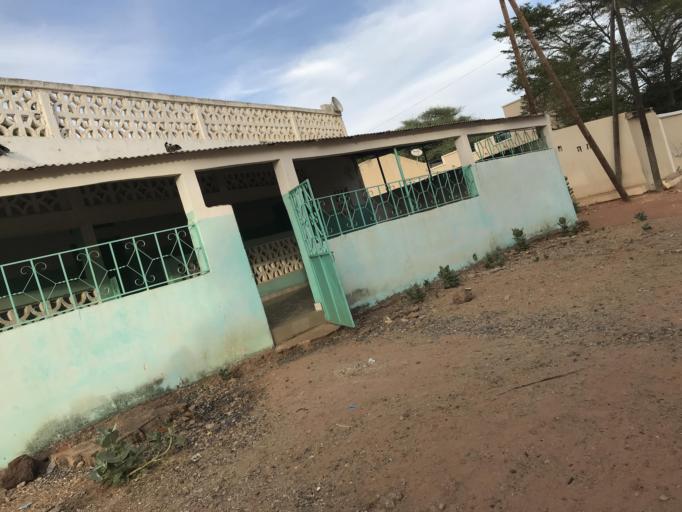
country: SN
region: Louga
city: Ndibene Dahra
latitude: 15.3988
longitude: -15.1174
